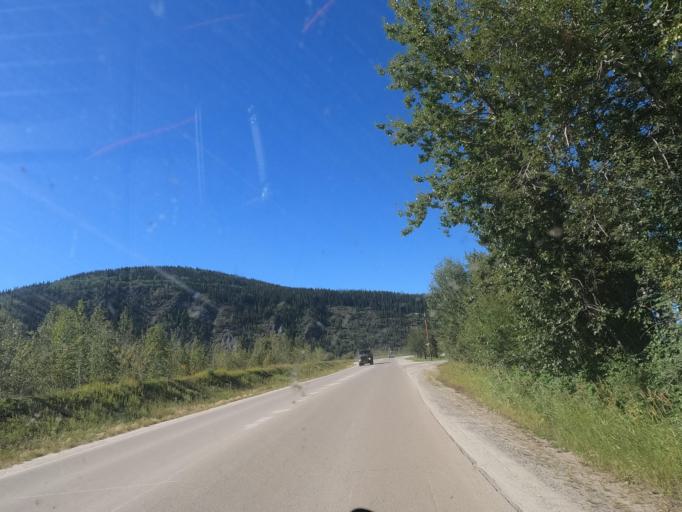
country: CA
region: Yukon
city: Dawson City
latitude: 64.0528
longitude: -139.4373
